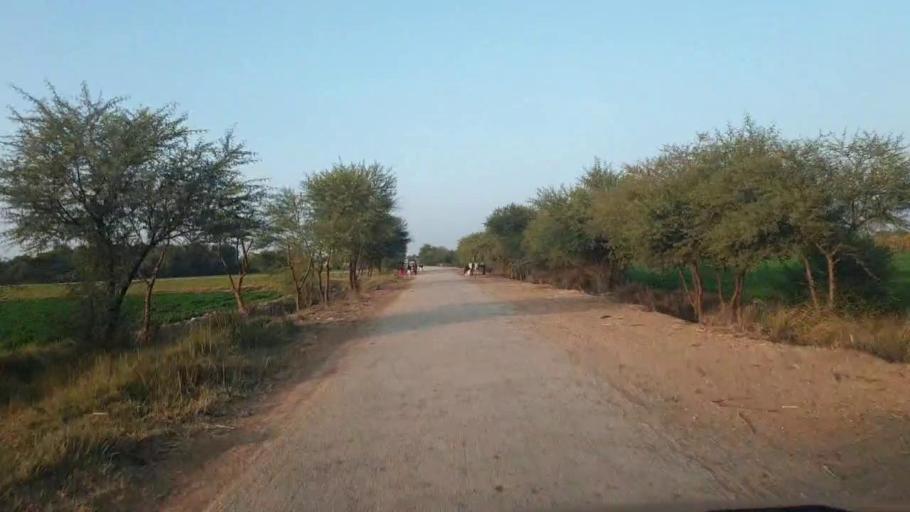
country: PK
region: Sindh
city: Berani
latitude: 25.8353
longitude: 68.7447
